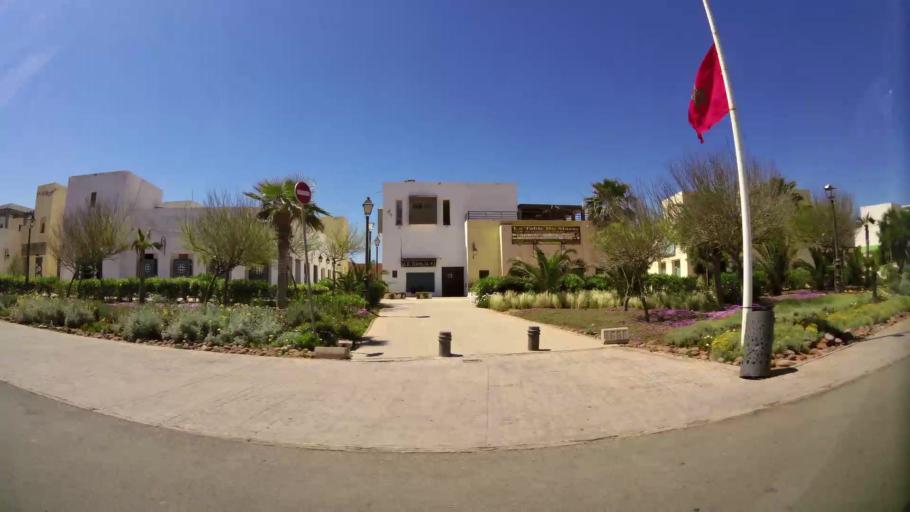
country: MA
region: Oriental
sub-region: Berkane-Taourirt
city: Madagh
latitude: 35.1089
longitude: -2.2963
